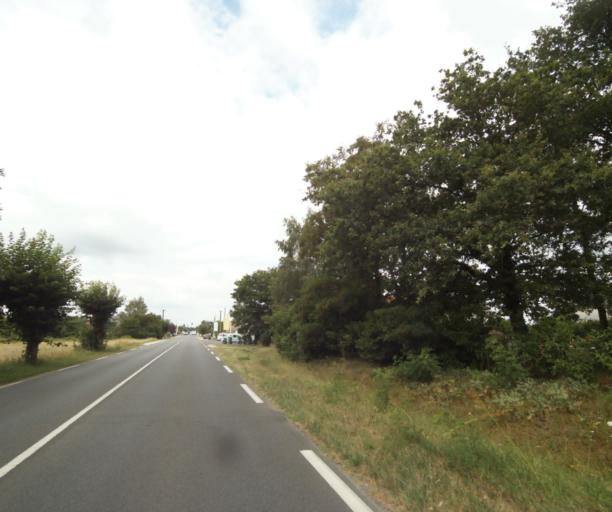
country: FR
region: Centre
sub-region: Departement du Loiret
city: Mardie
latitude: 47.8876
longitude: 2.0663
